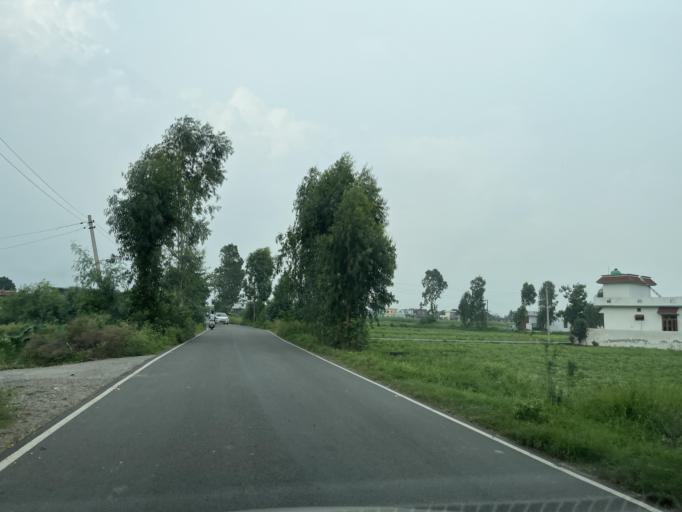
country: IN
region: Uttarakhand
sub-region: Naini Tal
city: Haldwani
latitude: 29.1772
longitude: 79.4714
